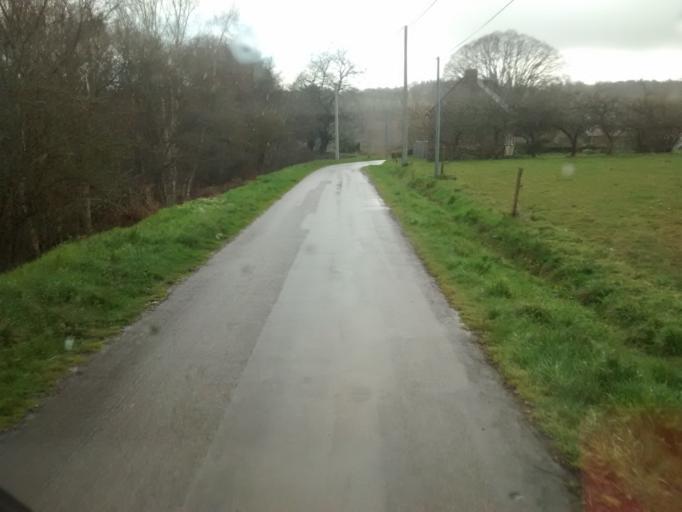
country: FR
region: Brittany
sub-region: Departement du Morbihan
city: Pluherlin
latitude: 47.7125
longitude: -2.3933
